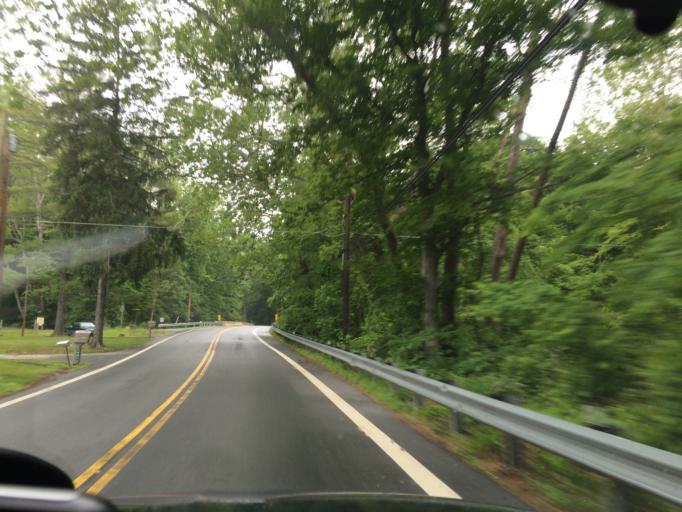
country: US
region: Maryland
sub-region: Frederick County
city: Thurmont
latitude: 39.6447
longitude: -77.4151
